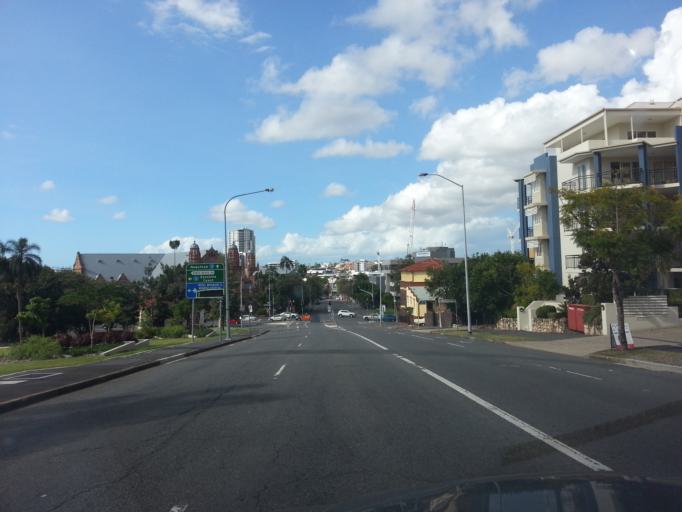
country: AU
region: Queensland
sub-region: Brisbane
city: Fortitude Valley
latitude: -27.4532
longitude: 153.0279
